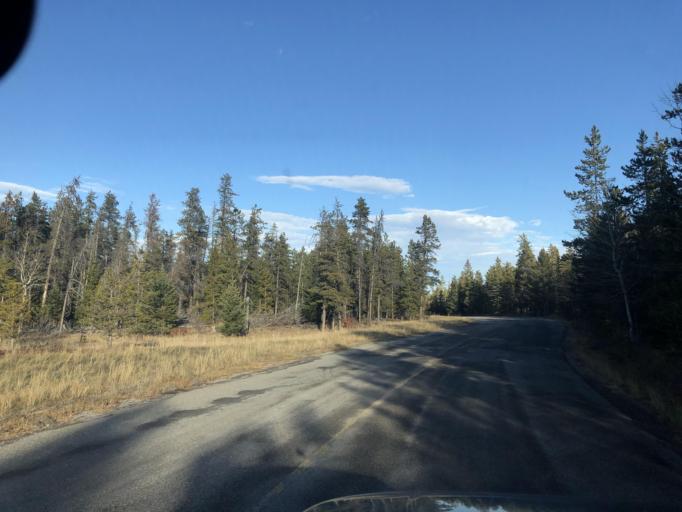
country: CA
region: Alberta
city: Canmore
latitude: 51.0753
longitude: -115.0702
